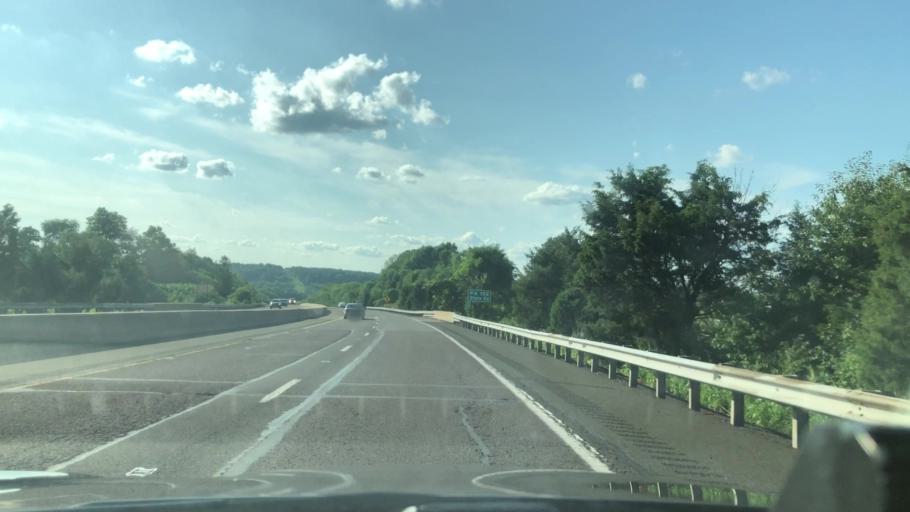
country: US
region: Pennsylvania
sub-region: Bucks County
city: Sellersville
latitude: 40.3423
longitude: -75.3171
